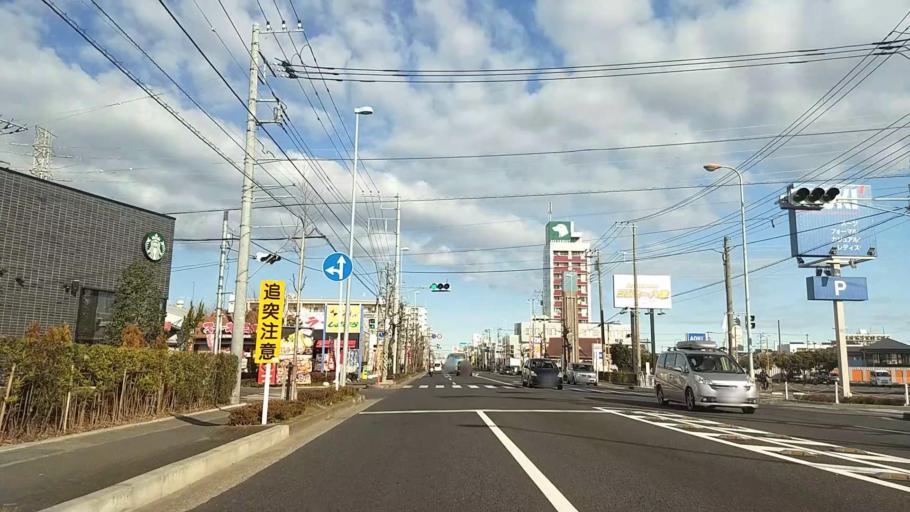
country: JP
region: Kanagawa
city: Hiratsuka
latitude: 35.3661
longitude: 139.3615
